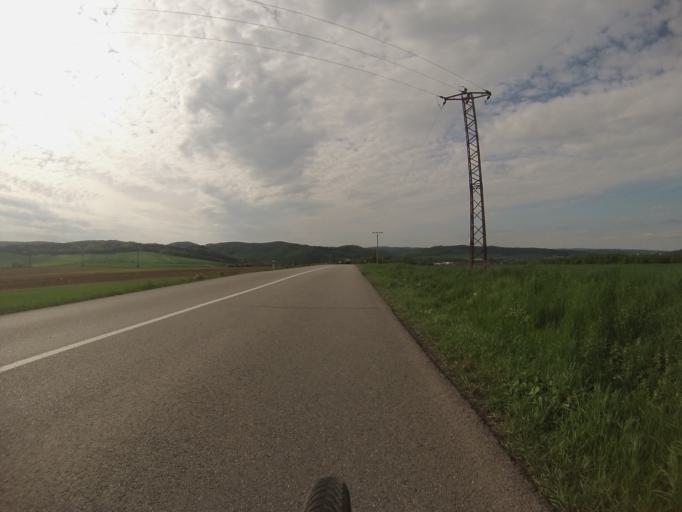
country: CZ
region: South Moravian
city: Veverska Bityska
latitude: 49.2583
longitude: 16.4469
